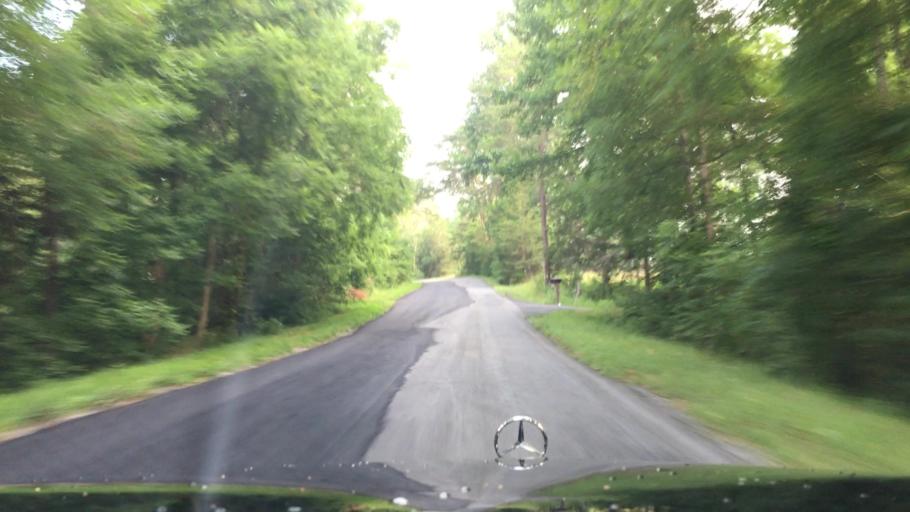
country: US
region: Virginia
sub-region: Campbell County
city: Timberlake
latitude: 37.2486
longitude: -79.3065
